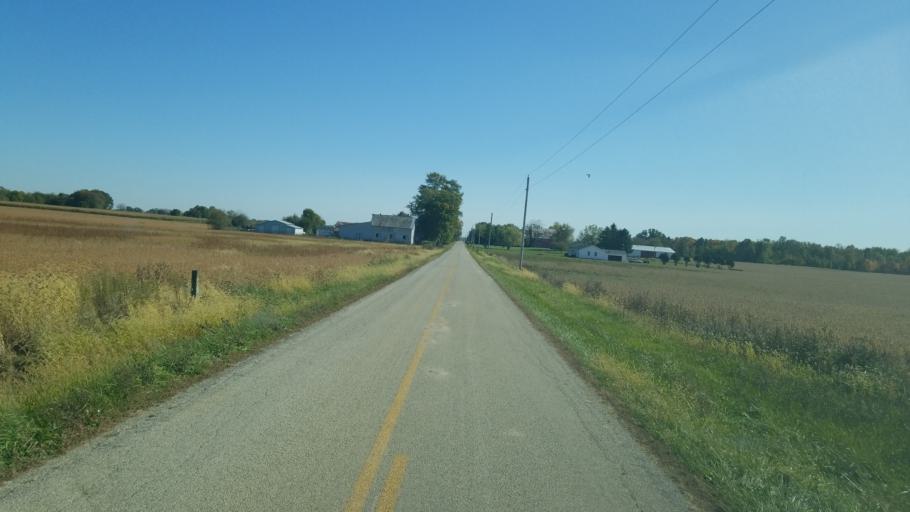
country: US
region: Ohio
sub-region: Marion County
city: Prospect
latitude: 40.5457
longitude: -83.2406
